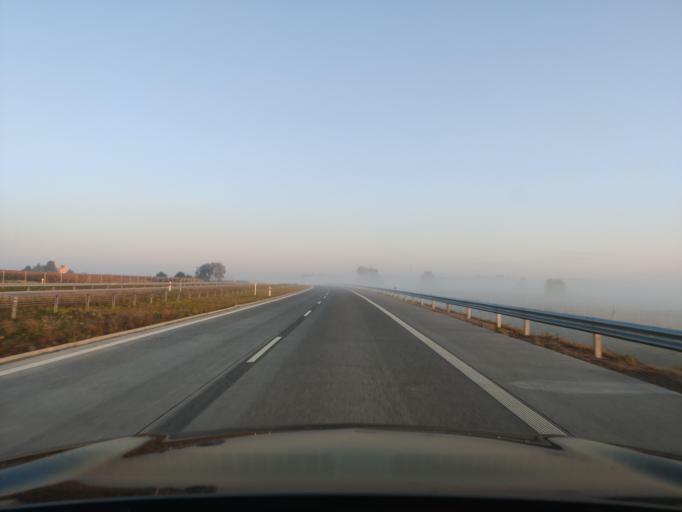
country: PL
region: Masovian Voivodeship
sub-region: Powiat mlawski
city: Wisniewo
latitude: 52.9978
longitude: 20.3453
